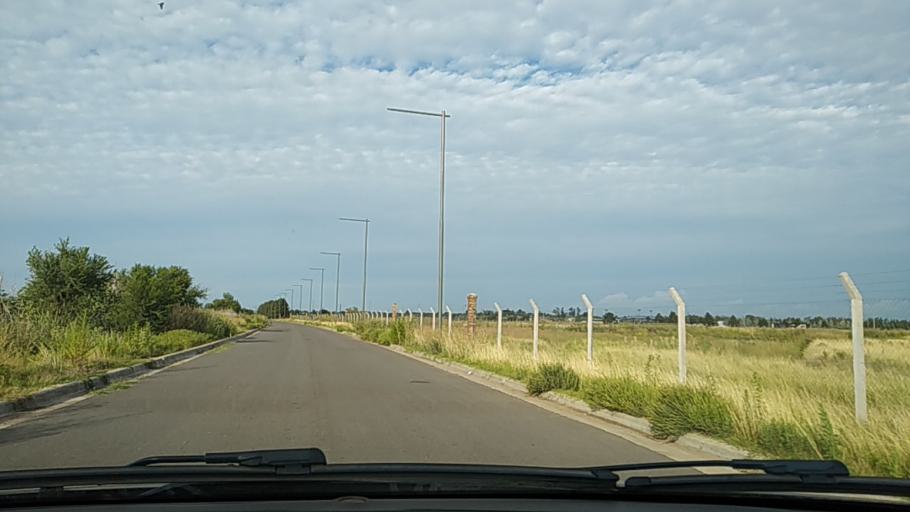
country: AR
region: Santa Fe
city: Funes
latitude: -32.9434
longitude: -60.7753
